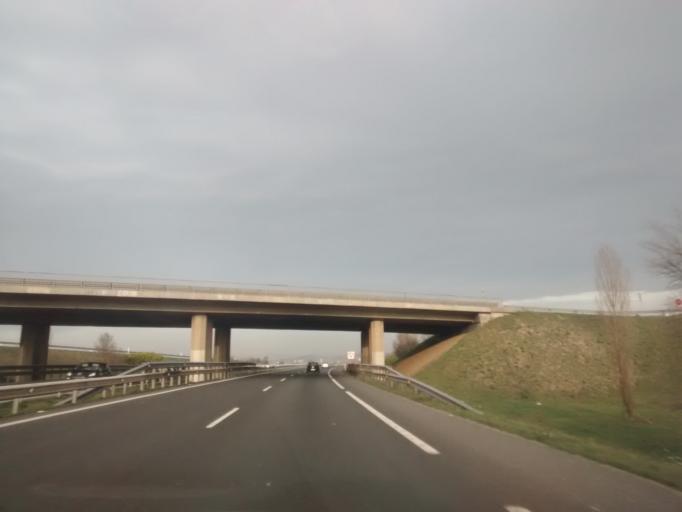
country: ES
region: Basque Country
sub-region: Provincia de Alava
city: Gasteiz / Vitoria
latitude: 42.8610
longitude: -2.7397
